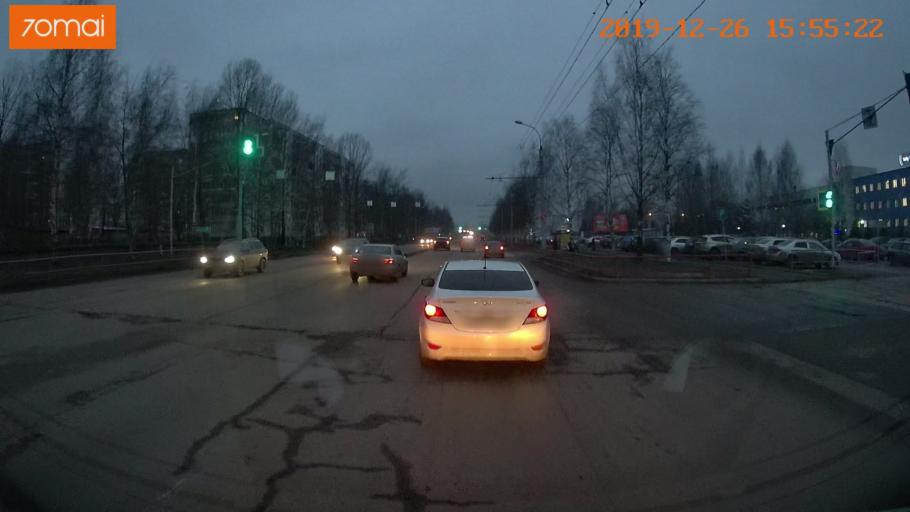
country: RU
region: Jaroslavl
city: Rybinsk
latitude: 58.0434
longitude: 38.8125
